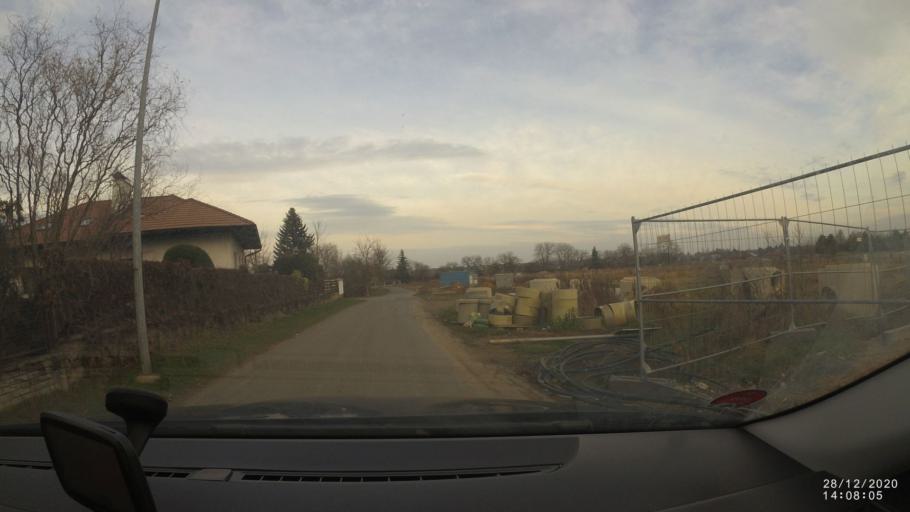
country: CZ
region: Central Bohemia
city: Sestajovice
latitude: 50.1024
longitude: 14.6625
